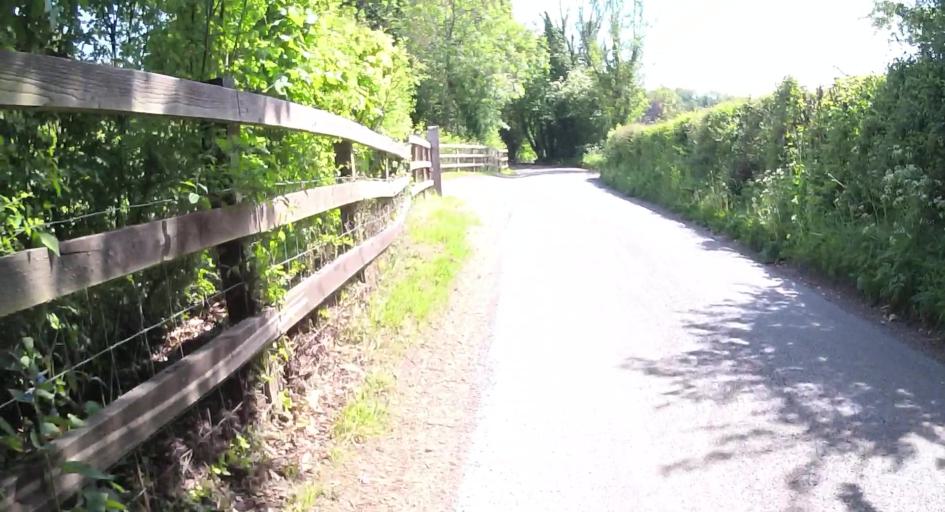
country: GB
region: England
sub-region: Hampshire
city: Kings Worthy
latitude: 51.0902
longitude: -1.1818
